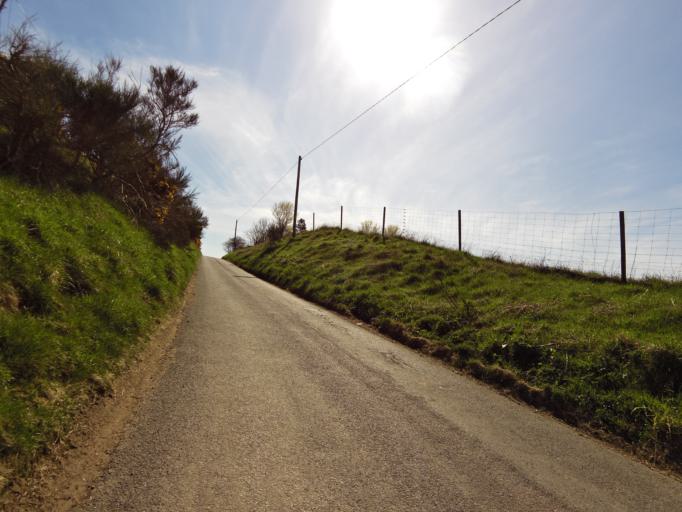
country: GB
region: Scotland
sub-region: Angus
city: Montrose
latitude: 56.6490
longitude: -2.5143
